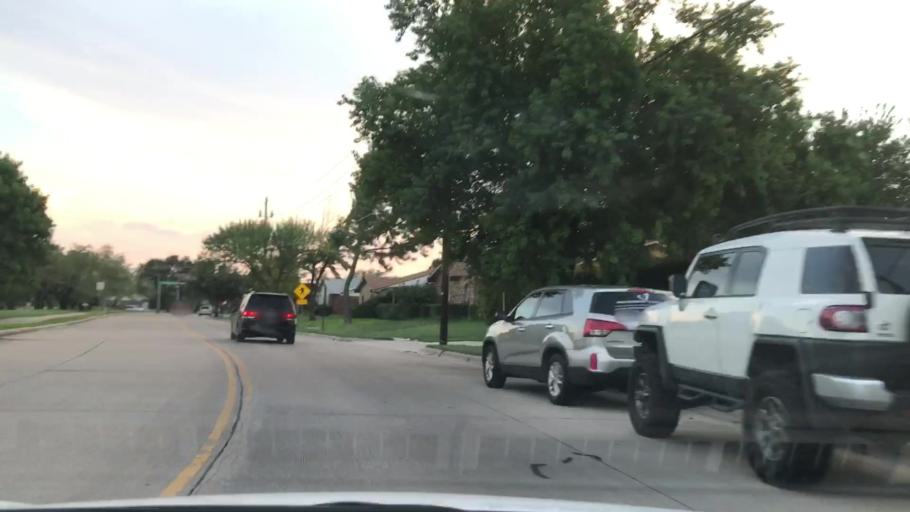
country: US
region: Texas
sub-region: Dallas County
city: Carrollton
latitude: 33.0011
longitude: -96.8787
